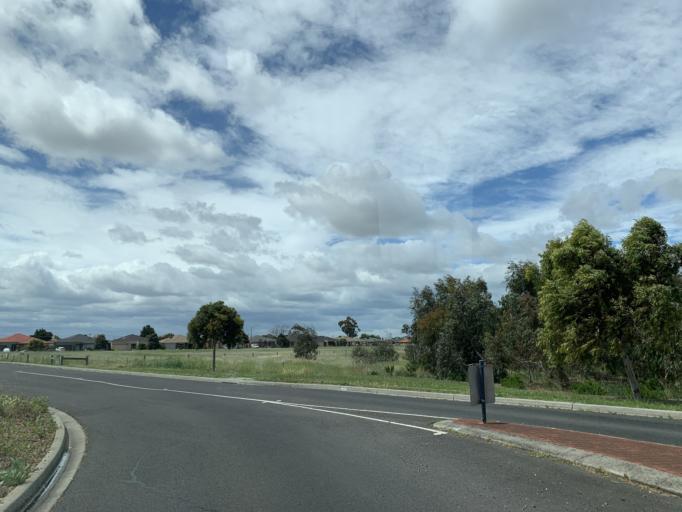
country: AU
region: Victoria
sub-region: Brimbank
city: Cairnlea
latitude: -37.7605
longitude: 144.7992
